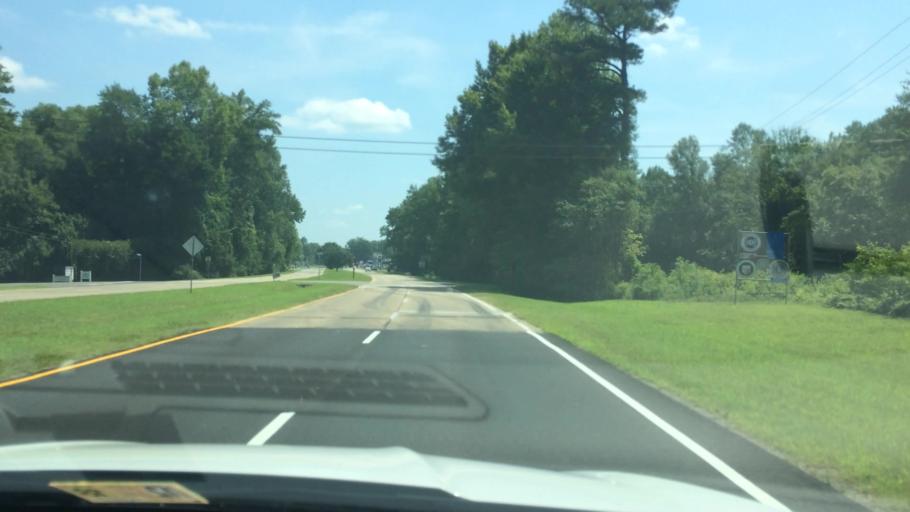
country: US
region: Virginia
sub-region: Charles City County
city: Charles City
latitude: 37.4427
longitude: -77.0487
